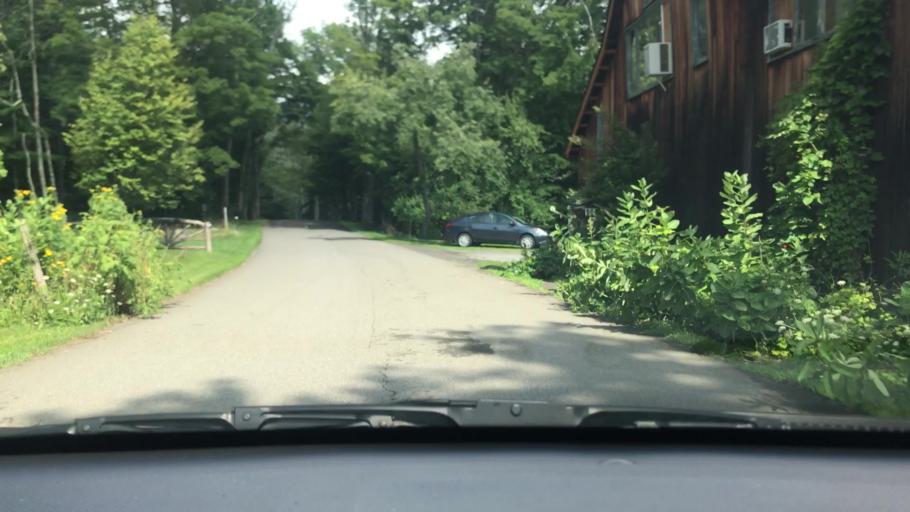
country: US
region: New York
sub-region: Ulster County
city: Shokan
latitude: 41.9605
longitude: -74.2801
